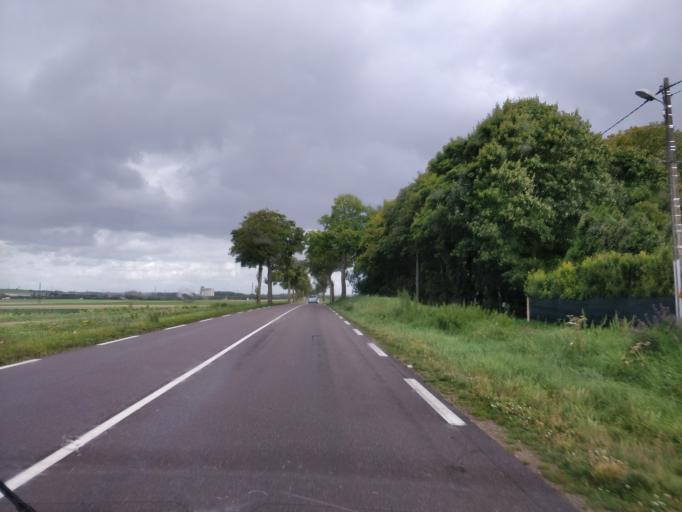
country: FR
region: Champagne-Ardenne
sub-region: Departement de l'Aube
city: Saint-Parres-aux-Tertres
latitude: 48.2944
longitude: 4.1423
